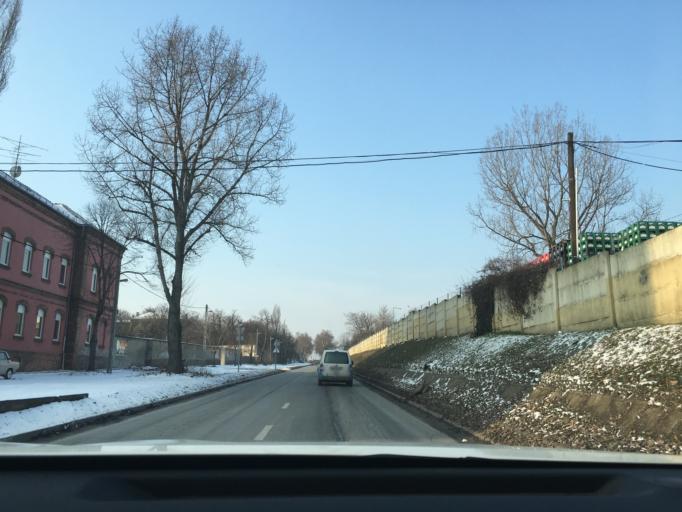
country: HU
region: Budapest
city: Budapest X. keruelet
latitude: 47.4876
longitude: 19.1519
